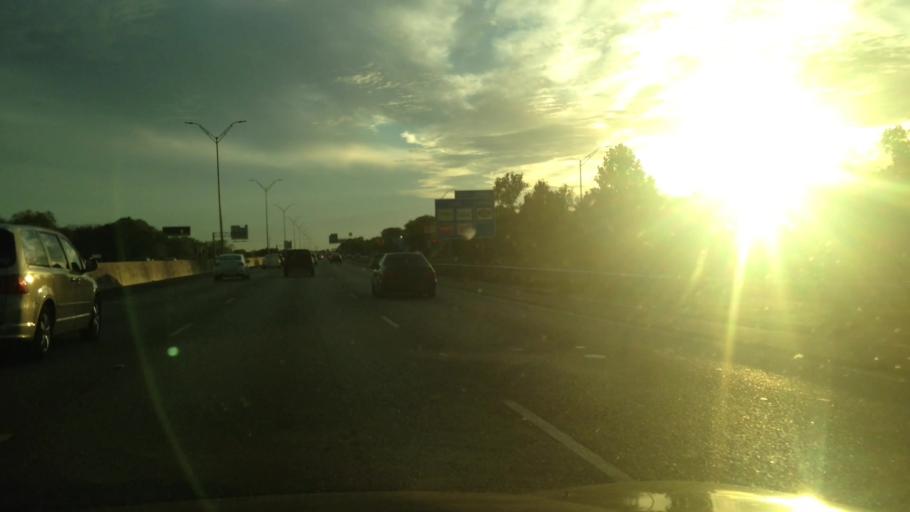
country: US
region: Texas
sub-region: Hays County
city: San Marcos
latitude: 29.8798
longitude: -97.9252
